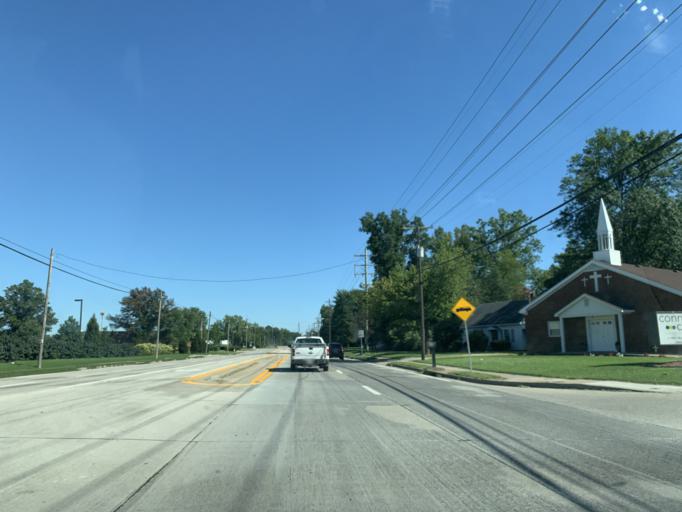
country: US
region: Kentucky
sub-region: Jefferson County
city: Audubon Park
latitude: 38.1815
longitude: -85.6964
